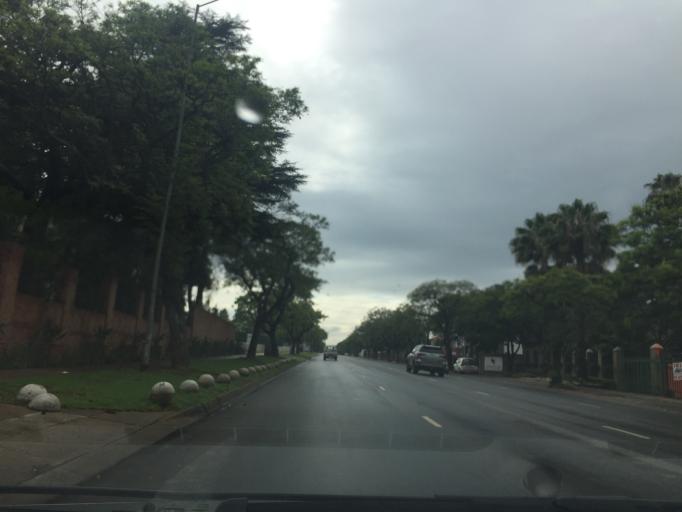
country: ZA
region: Gauteng
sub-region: City of Tshwane Metropolitan Municipality
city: Pretoria
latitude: -25.7470
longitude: 28.2226
